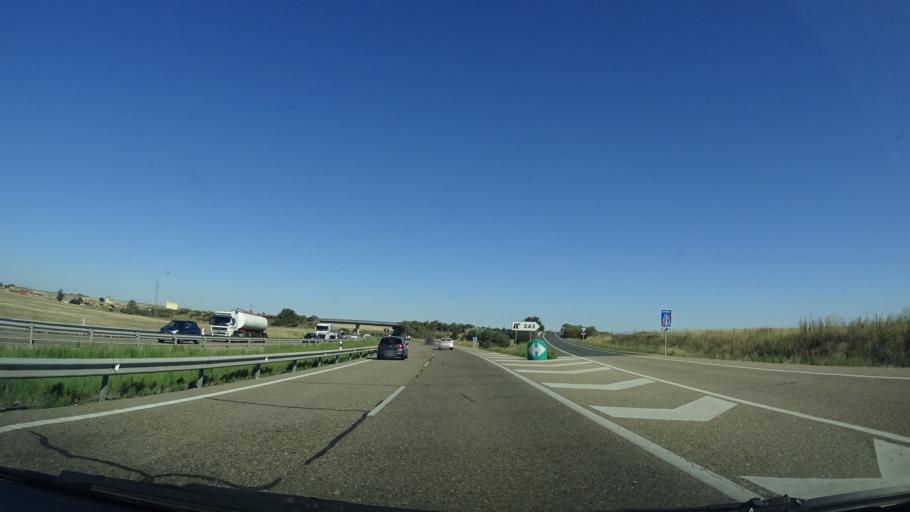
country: ES
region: Castille and Leon
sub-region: Provincia de Zamora
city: Cerecinos de Campos
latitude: 41.9001
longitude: -5.4754
